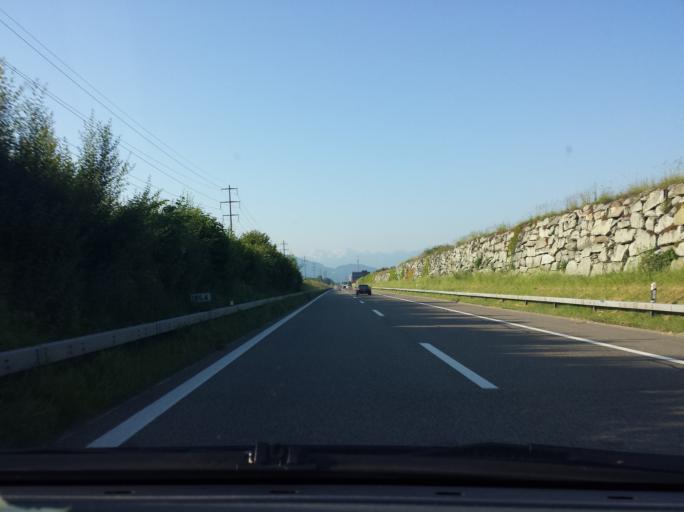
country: AT
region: Vorarlberg
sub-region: Politischer Bezirk Dornbirn
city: Lustenau
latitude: 47.4241
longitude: 9.6463
